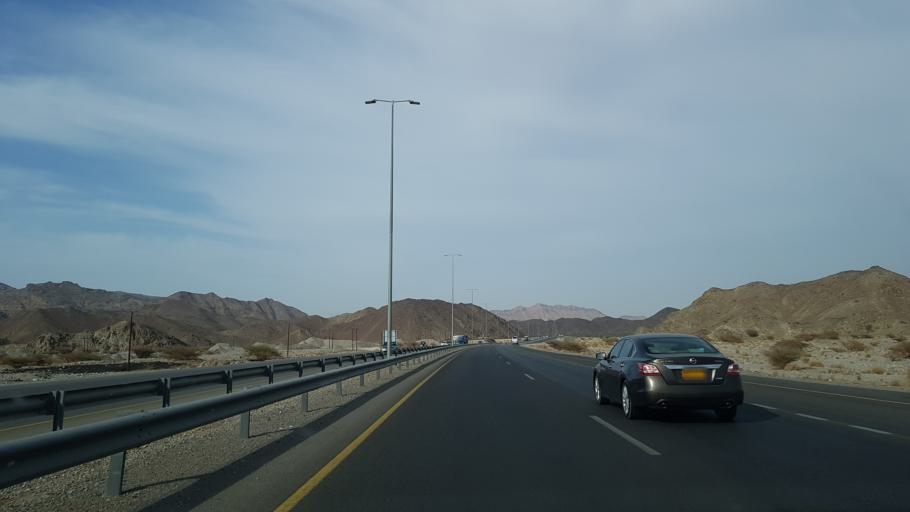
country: OM
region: Muhafazat ad Dakhiliyah
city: Bidbid
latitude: 23.3893
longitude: 58.0621
